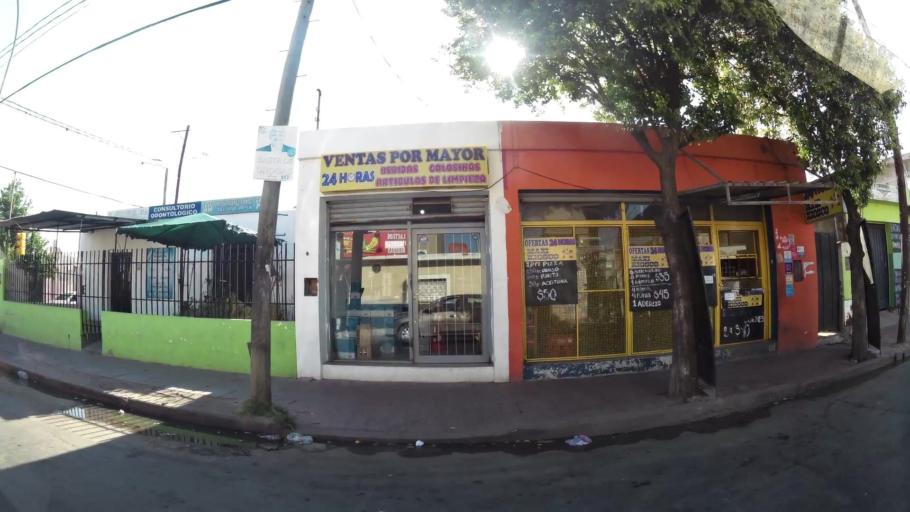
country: AR
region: Cordoba
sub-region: Departamento de Capital
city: Cordoba
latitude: -31.4721
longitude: -64.2246
